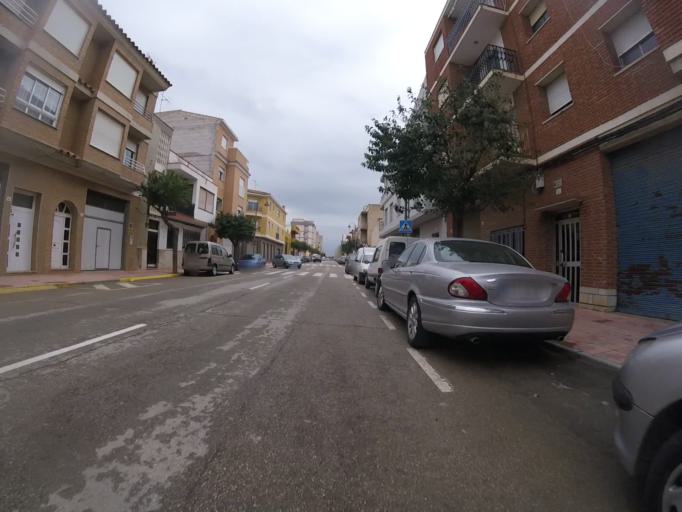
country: ES
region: Valencia
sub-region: Provincia de Castello
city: Alcala de Xivert
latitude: 40.3029
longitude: 0.2268
